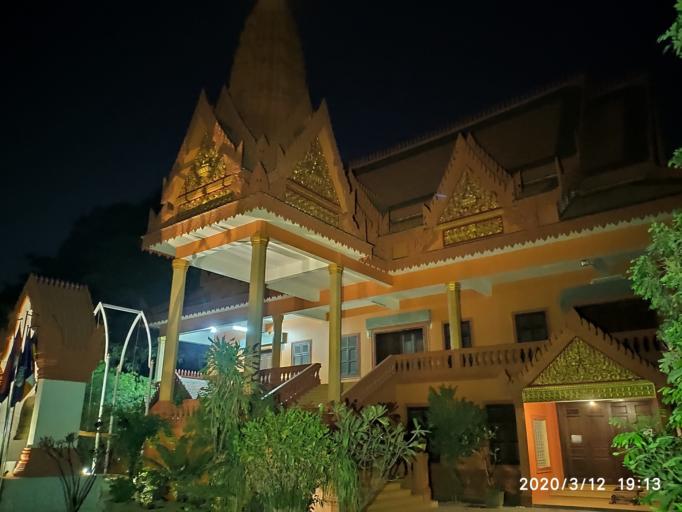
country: KH
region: Siem Reap
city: Siem Reap
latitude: 13.3564
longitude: 103.8622
